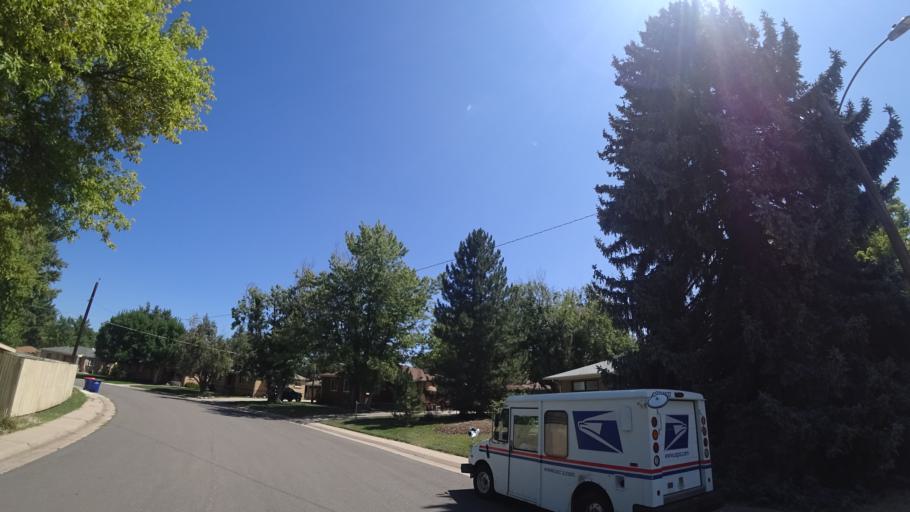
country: US
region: Colorado
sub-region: Arapahoe County
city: Littleton
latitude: 39.6121
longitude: -104.9944
